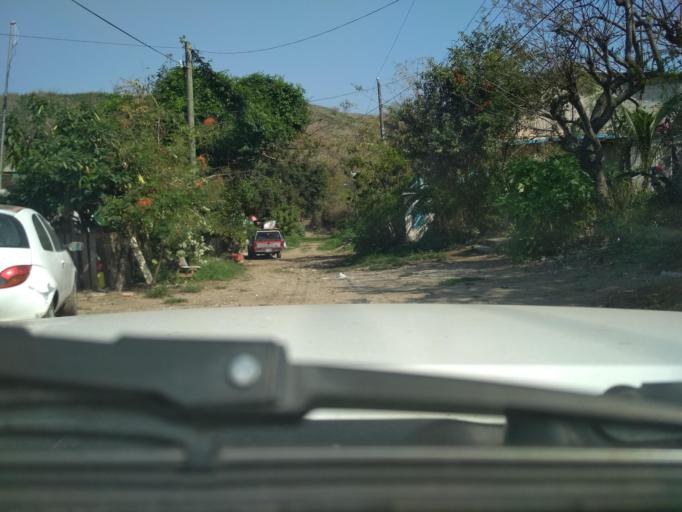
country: MX
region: Veracruz
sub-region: Veracruz
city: Colonia el Renacimiento
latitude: 19.2204
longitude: -96.2141
